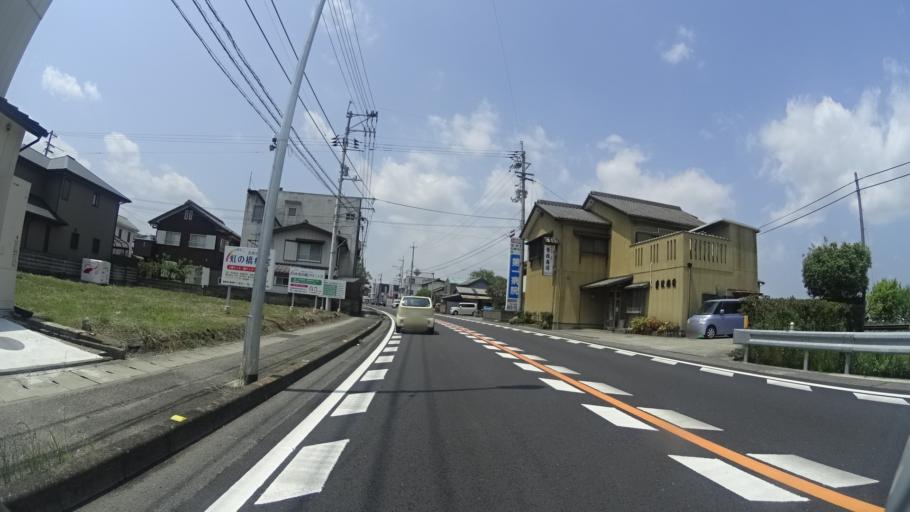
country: JP
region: Tokushima
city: Ishii
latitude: 34.0675
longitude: 134.4241
